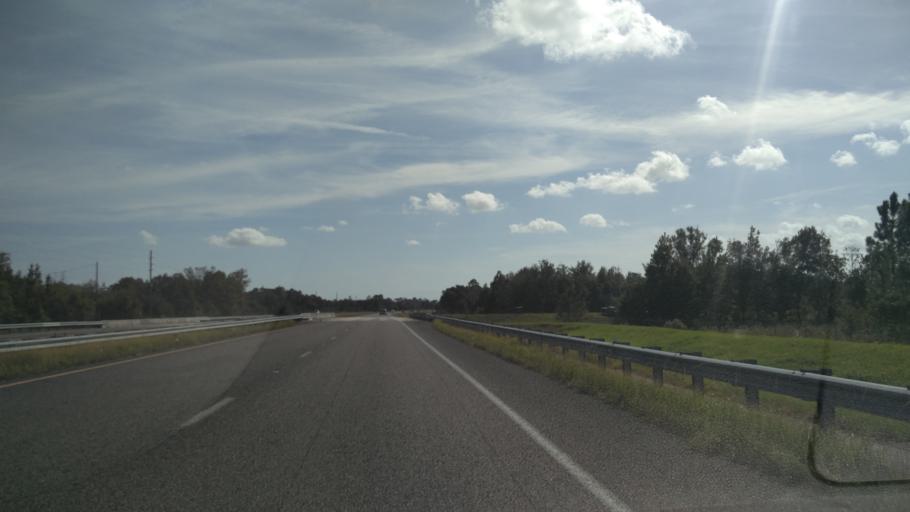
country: US
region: Florida
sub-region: Brevard County
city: June Park
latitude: 28.1175
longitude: -80.9341
